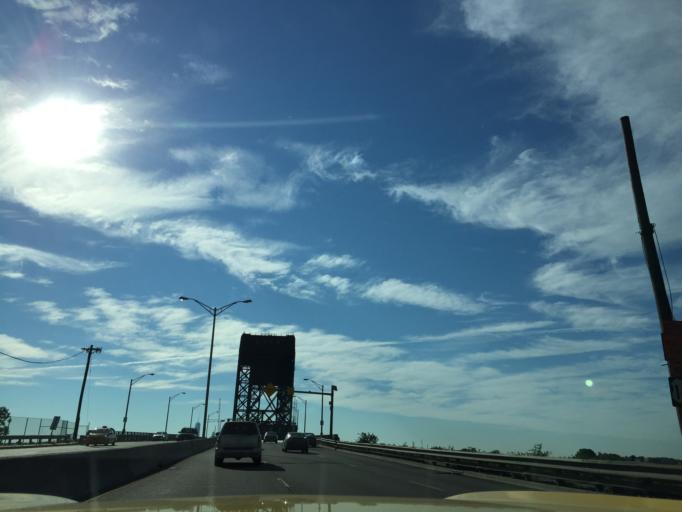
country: US
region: New Jersey
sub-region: Hudson County
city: Jersey City
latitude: 40.7284
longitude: -74.1028
